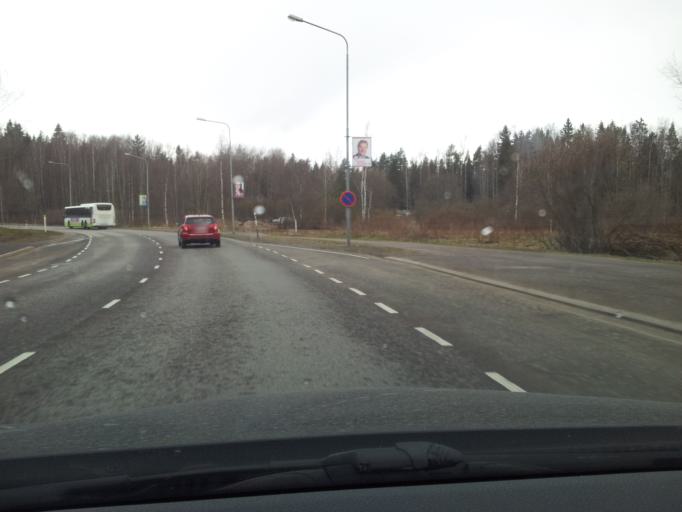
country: FI
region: Uusimaa
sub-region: Helsinki
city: Kauniainen
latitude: 60.1766
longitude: 24.7174
